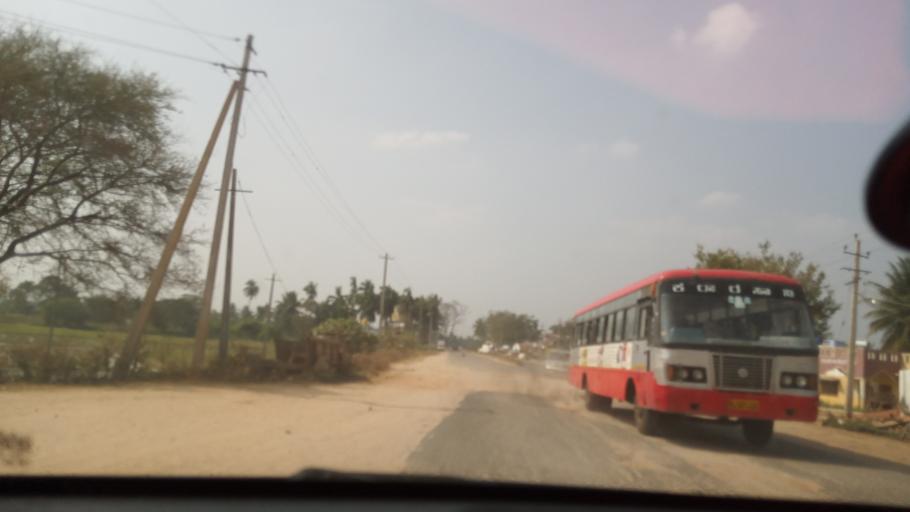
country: IN
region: Karnataka
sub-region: Mysore
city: Nanjangud
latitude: 12.1116
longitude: 76.7039
